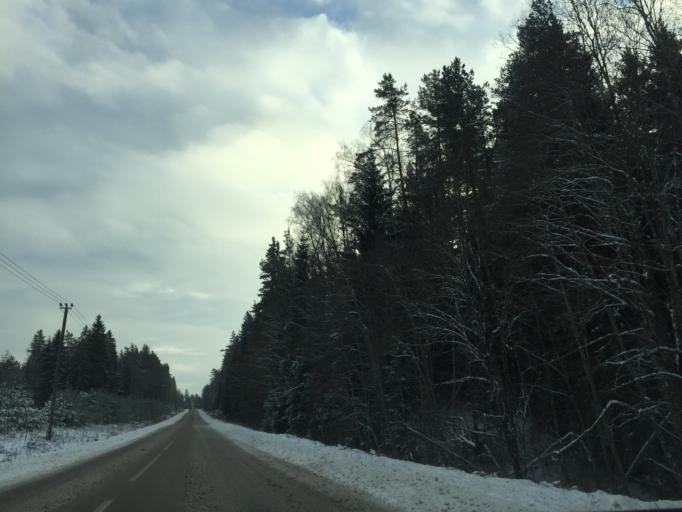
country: LV
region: Amatas Novads
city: Drabesi
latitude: 57.2181
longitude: 25.2917
